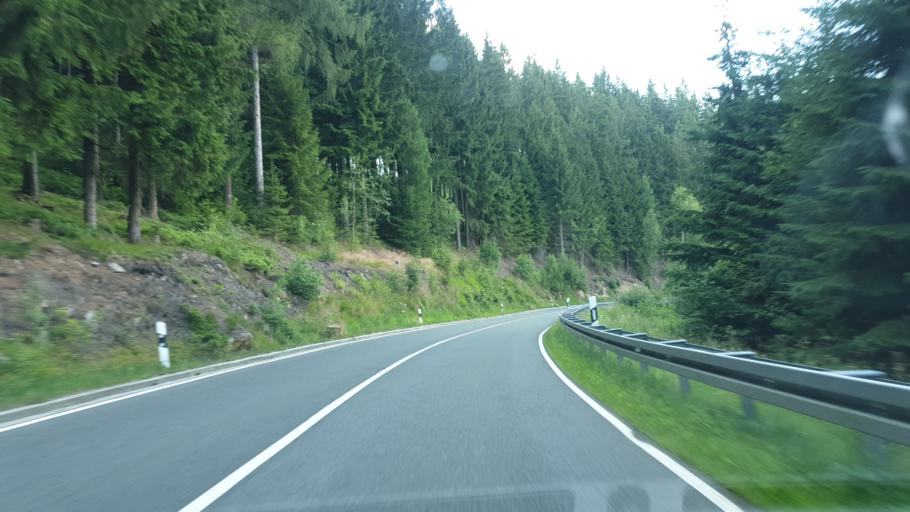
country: DE
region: Saxony
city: Tannenbergsthal
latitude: 50.4524
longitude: 12.4376
